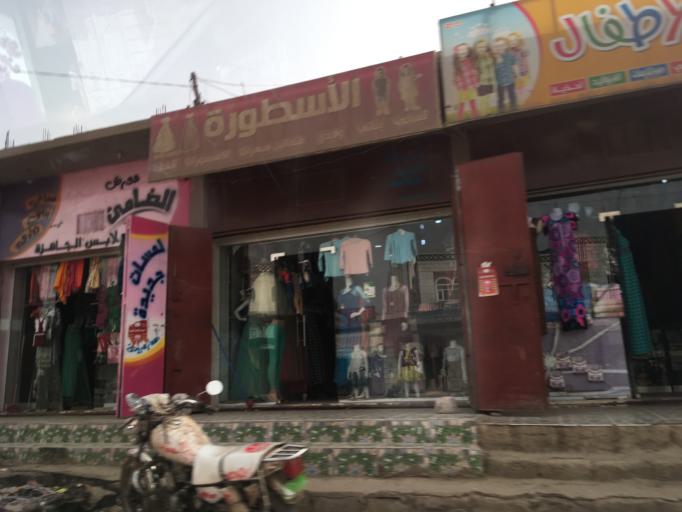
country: YE
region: Ad Dali'
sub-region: Ad Dhale'e
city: Dhalie
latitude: 13.7044
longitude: 44.7353
